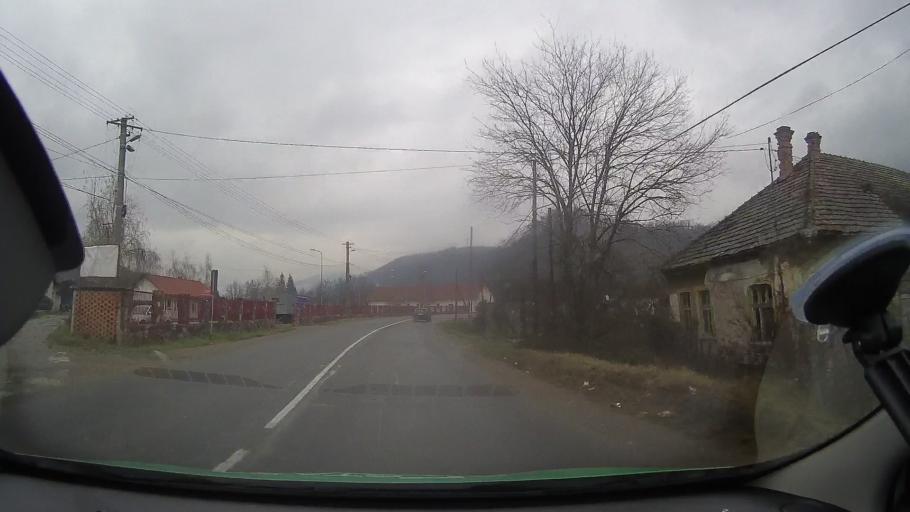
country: RO
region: Arad
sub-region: Comuna Gurahont
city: Gurahont
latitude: 46.2760
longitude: 22.3391
